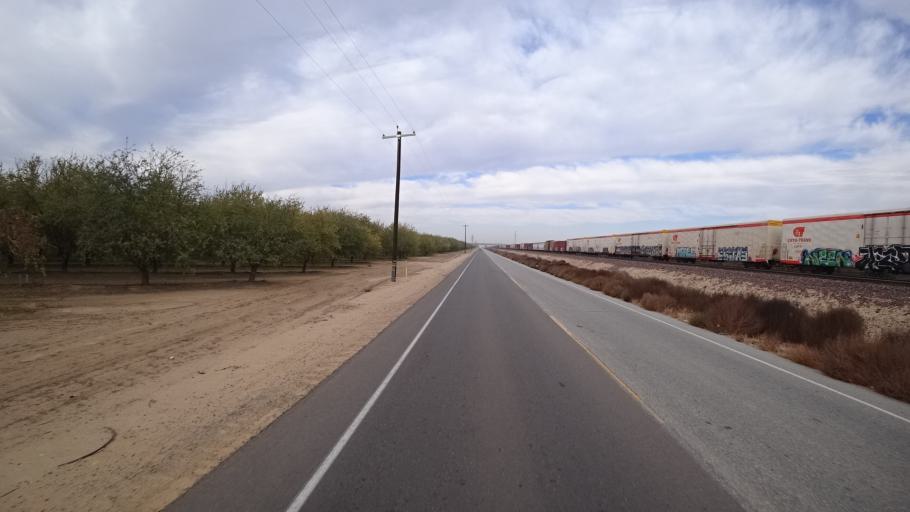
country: US
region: California
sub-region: Kern County
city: Rosedale
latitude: 35.4352
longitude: -119.1913
